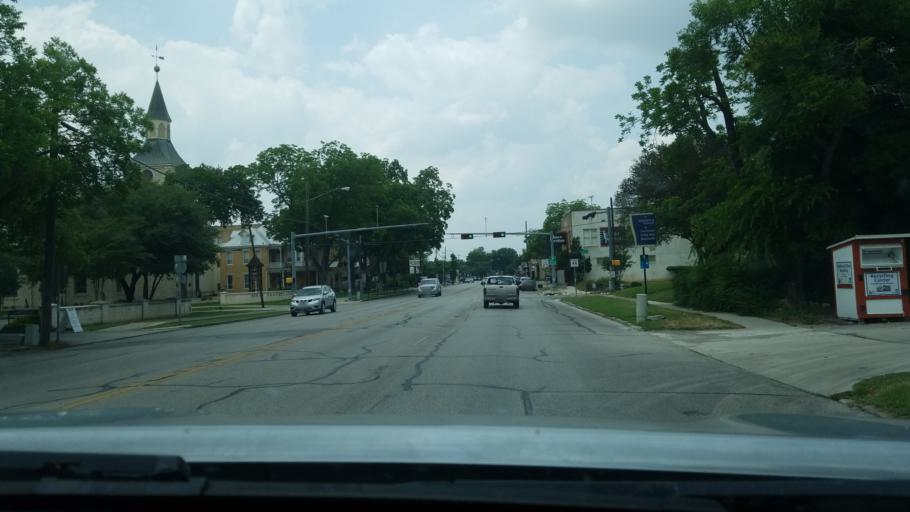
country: US
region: Texas
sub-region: Comal County
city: New Braunfels
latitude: 29.7009
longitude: -98.1215
